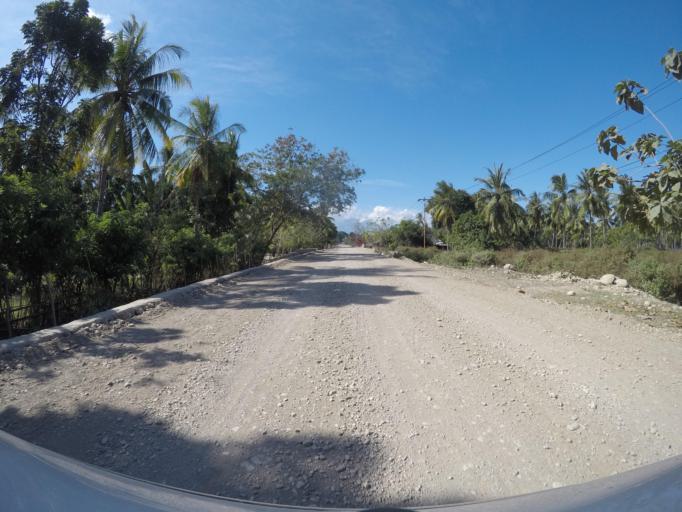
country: TL
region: Viqueque
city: Viqueque
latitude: -8.8550
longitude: 126.5111
